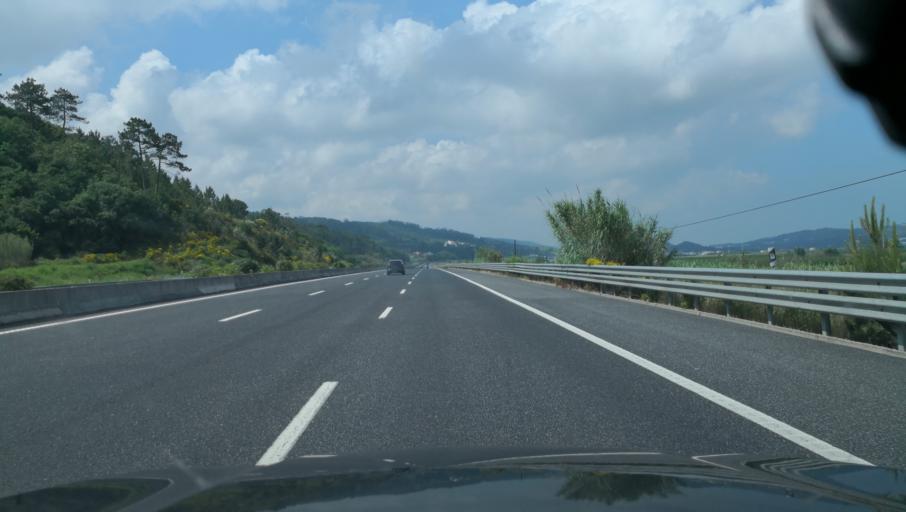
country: PT
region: Leiria
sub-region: Nazare
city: Nazare
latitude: 39.5671
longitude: -9.0398
